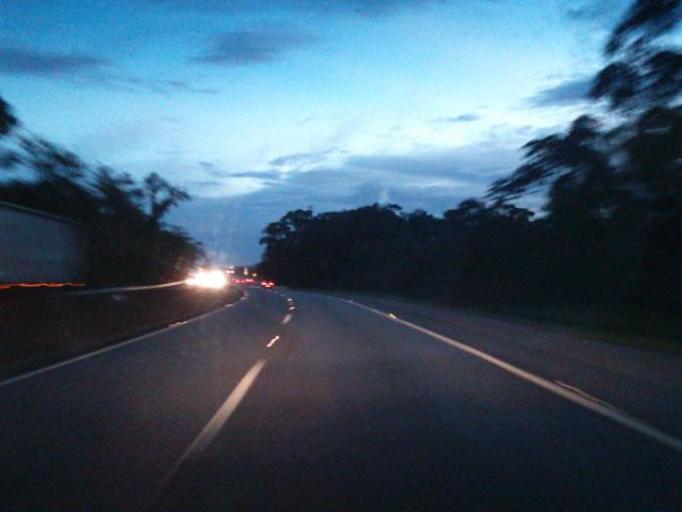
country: BR
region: Santa Catarina
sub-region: Barra Velha
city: Barra Velha
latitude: -26.5742
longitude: -48.7229
